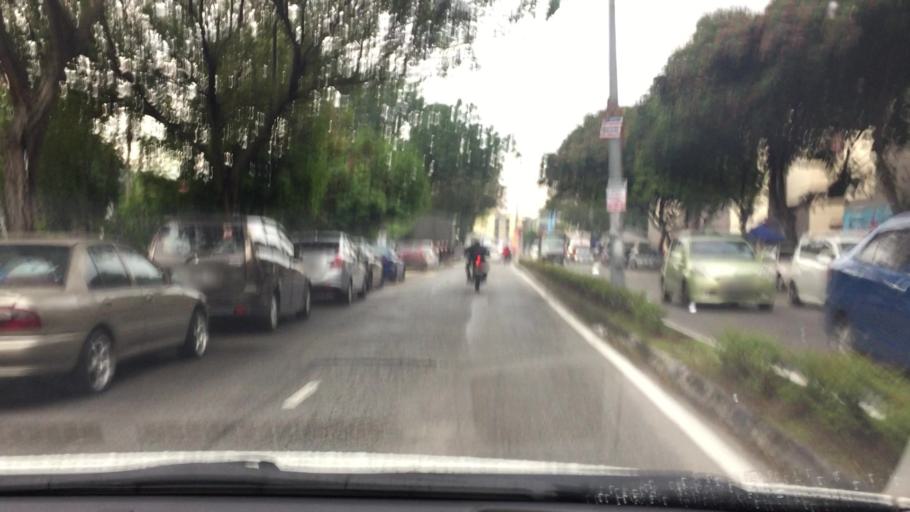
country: MY
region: Selangor
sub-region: Petaling
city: Petaling Jaya
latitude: 3.0776
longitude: 101.6442
